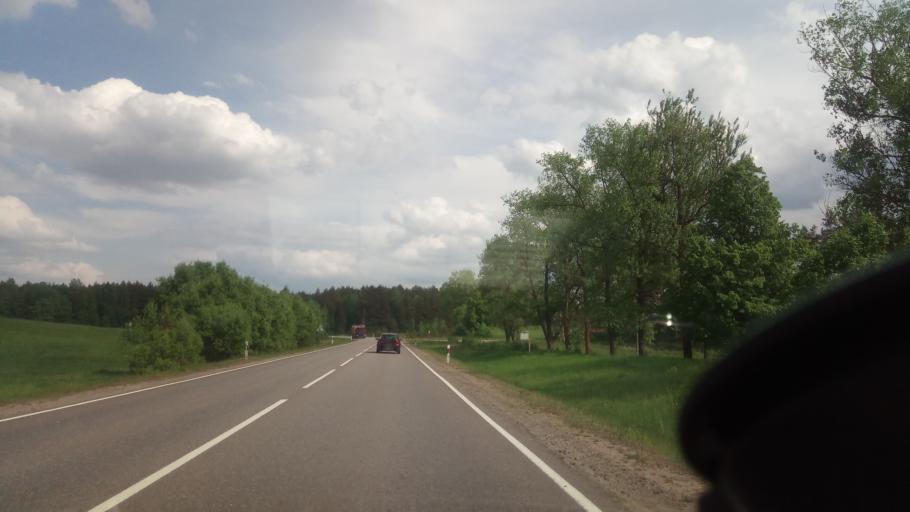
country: LT
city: Trakai
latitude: 54.6063
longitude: 24.8470
